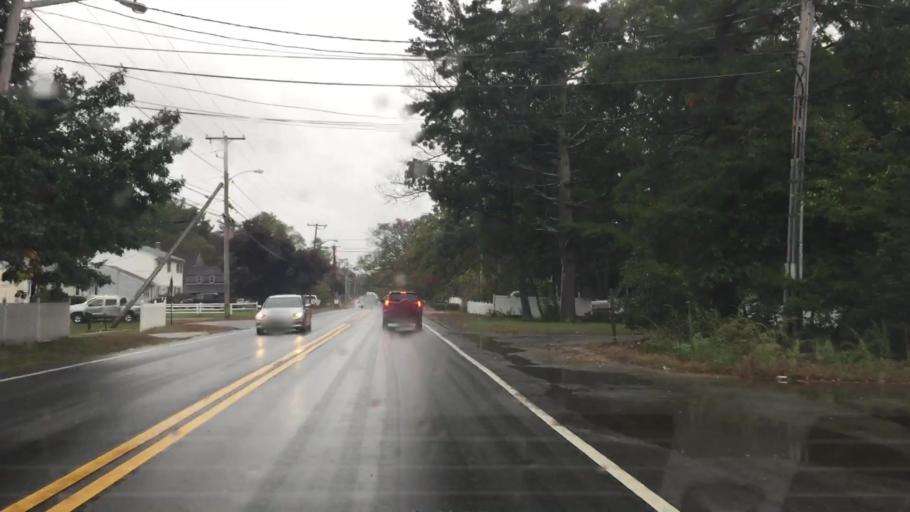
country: US
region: New Hampshire
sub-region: Rockingham County
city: Seabrook
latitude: 42.8733
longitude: -70.8752
